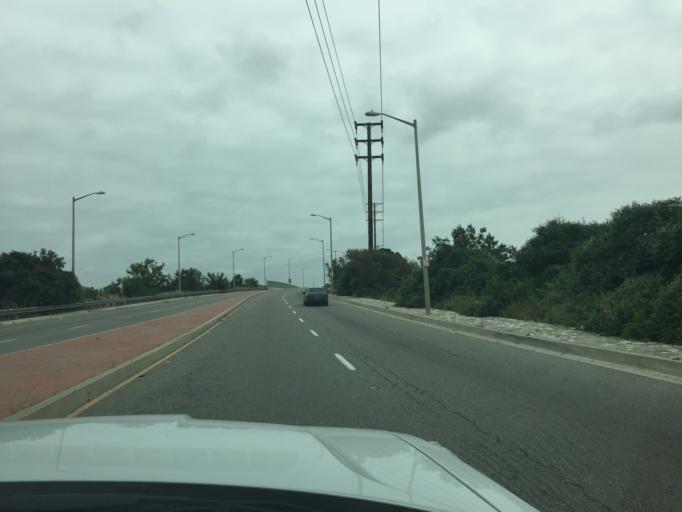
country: US
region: California
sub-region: Los Angeles County
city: Carson
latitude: 33.8318
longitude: -118.2287
